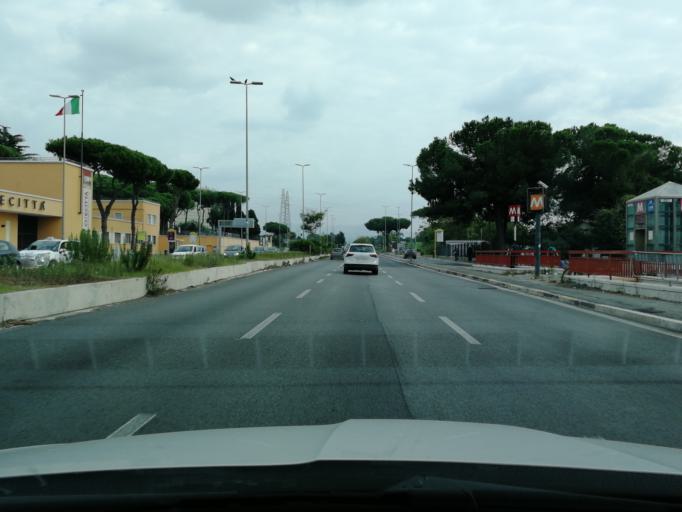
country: IT
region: Latium
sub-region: Citta metropolitana di Roma Capitale
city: Ciampino
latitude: 41.8496
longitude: 12.5738
